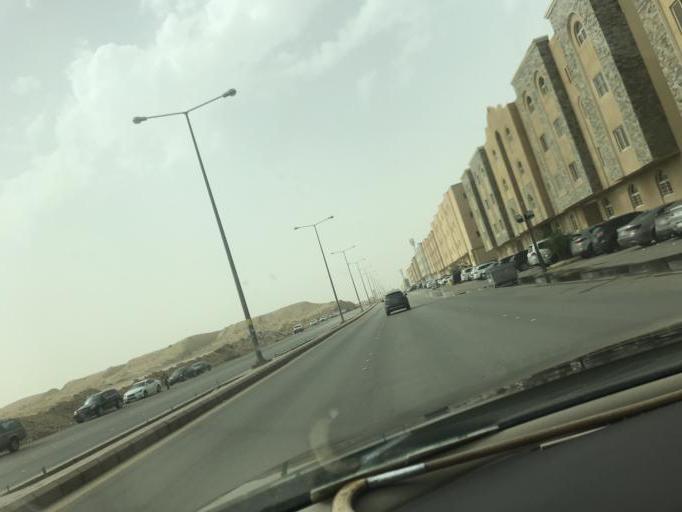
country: SA
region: Ar Riyad
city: Riyadh
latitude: 24.7916
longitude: 46.6697
